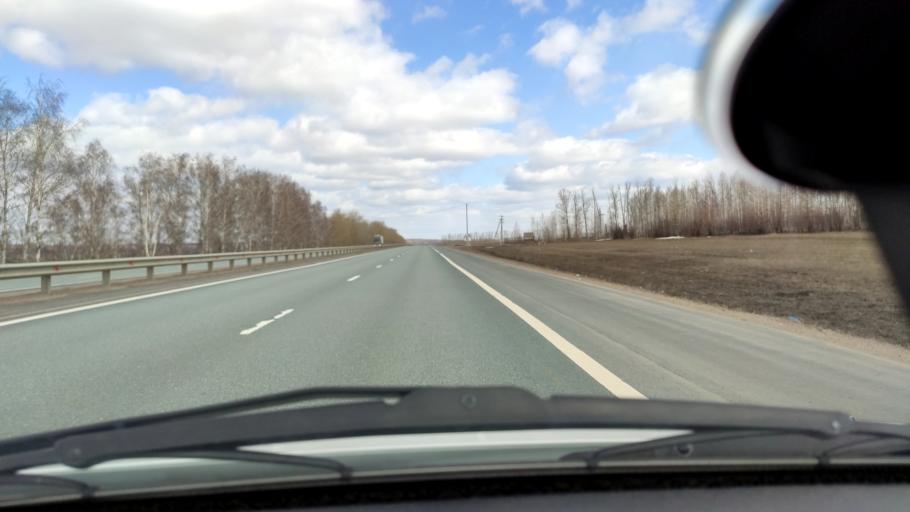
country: RU
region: Bashkortostan
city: Tolbazy
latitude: 54.3170
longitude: 55.8886
